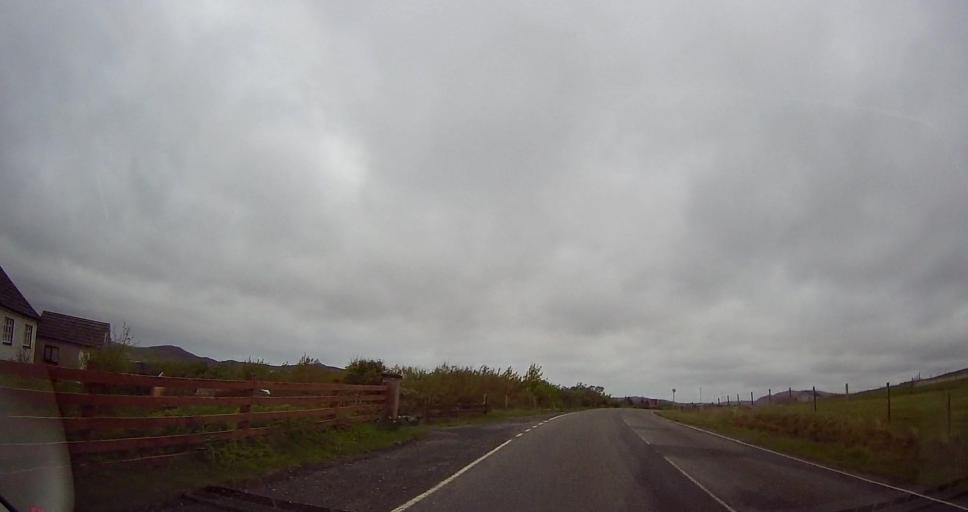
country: GB
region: Scotland
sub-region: Shetland Islands
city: Lerwick
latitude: 60.3862
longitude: -1.3445
